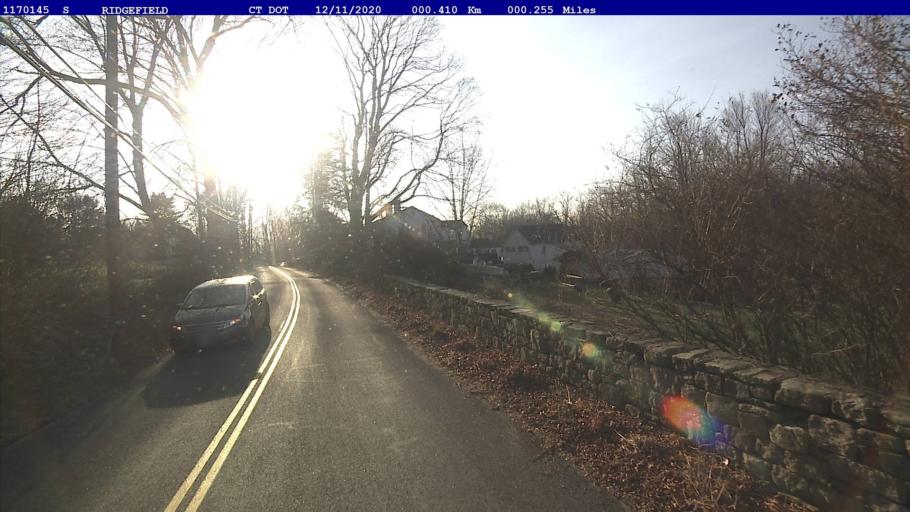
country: US
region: Connecticut
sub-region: Fairfield County
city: Ridgefield
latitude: 41.2658
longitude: -73.4798
